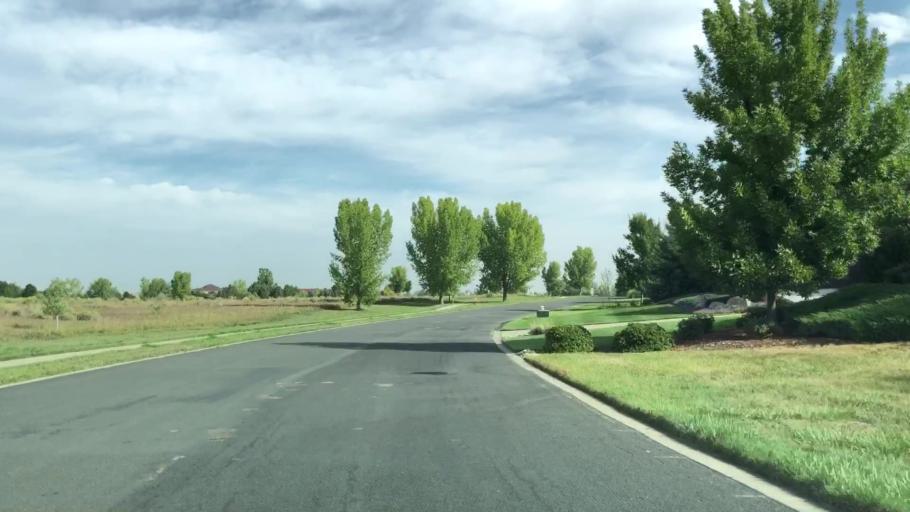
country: US
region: Colorado
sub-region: Larimer County
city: Loveland
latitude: 40.4352
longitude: -105.0531
